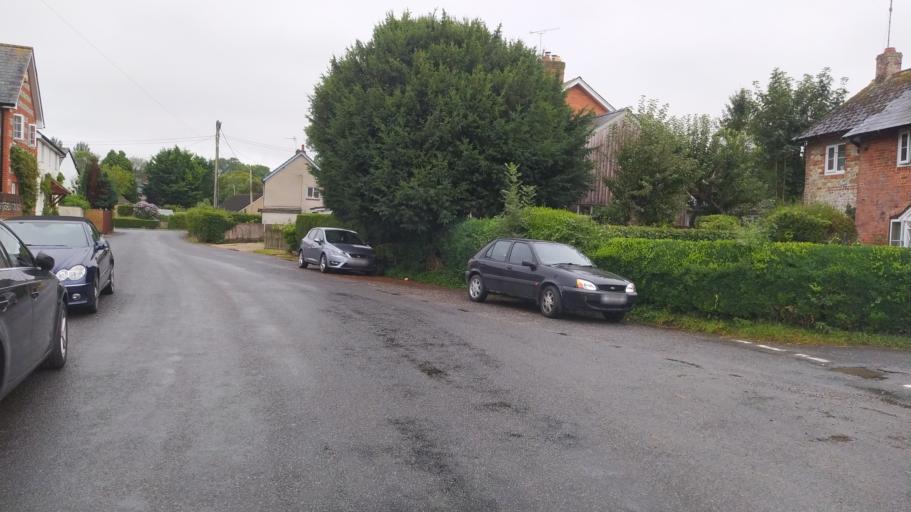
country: GB
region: England
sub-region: Wiltshire
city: Bower Chalke
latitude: 51.0301
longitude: -1.9464
